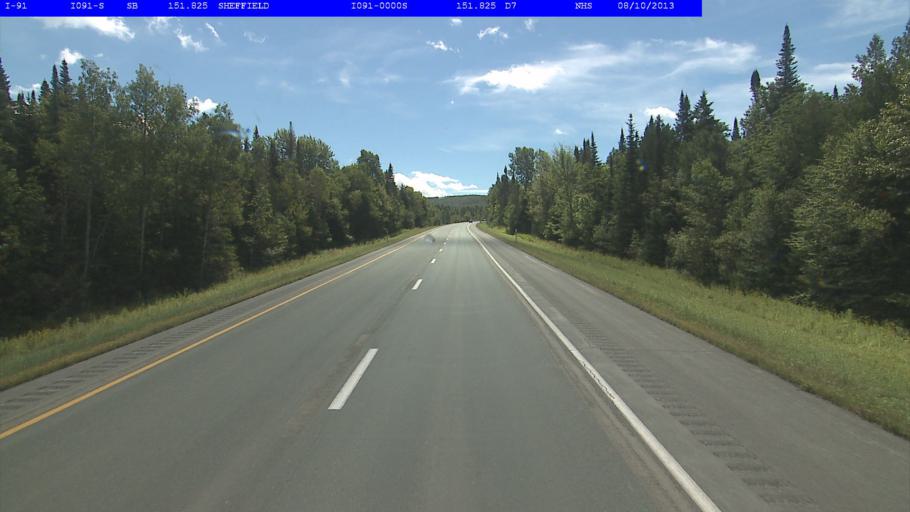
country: US
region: Vermont
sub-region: Caledonia County
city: Lyndonville
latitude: 44.6904
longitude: -72.1383
